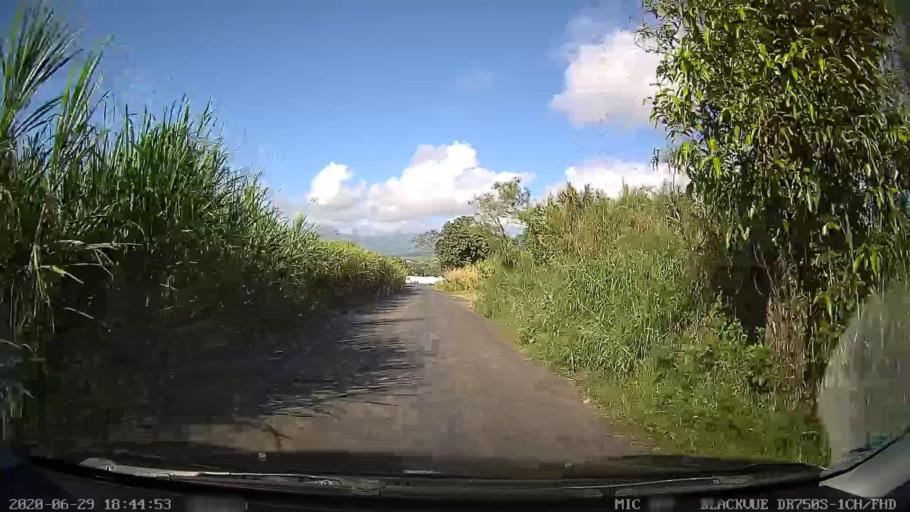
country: RE
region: Reunion
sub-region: Reunion
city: Bras-Panon
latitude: -20.9975
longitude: 55.6855
